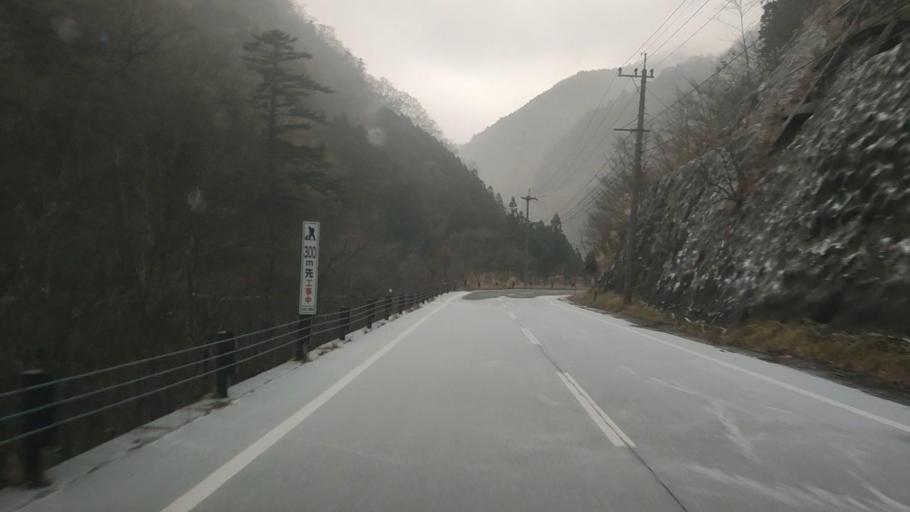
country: JP
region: Kumamoto
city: Matsubase
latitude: 32.5587
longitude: 130.9191
